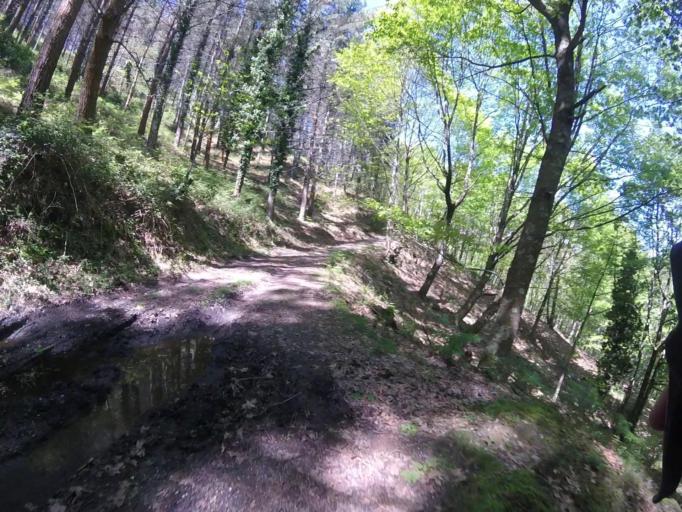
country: ES
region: Navarre
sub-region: Provincia de Navarra
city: Lesaka
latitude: 43.2470
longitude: -1.7520
